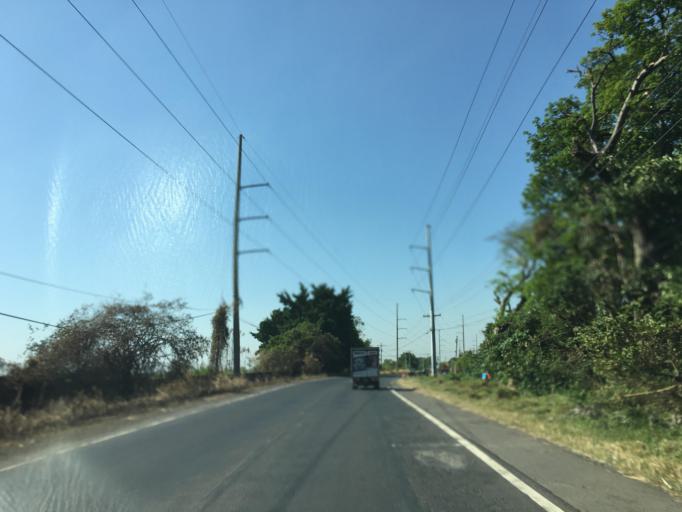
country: GT
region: Escuintla
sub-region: Municipio de Escuintla
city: Escuintla
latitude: 14.2598
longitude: -90.7980
